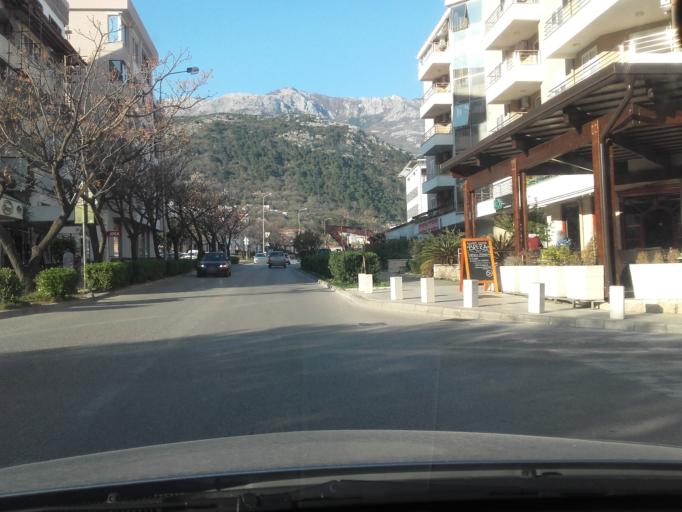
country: ME
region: Budva
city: Budva
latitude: 42.2925
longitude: 18.8382
